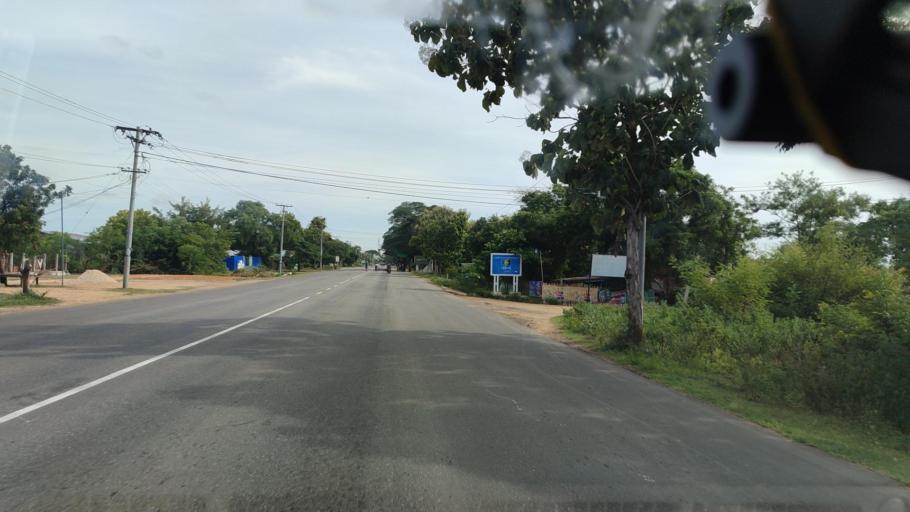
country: MM
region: Mandalay
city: Yamethin
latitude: 20.4028
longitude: 96.1448
